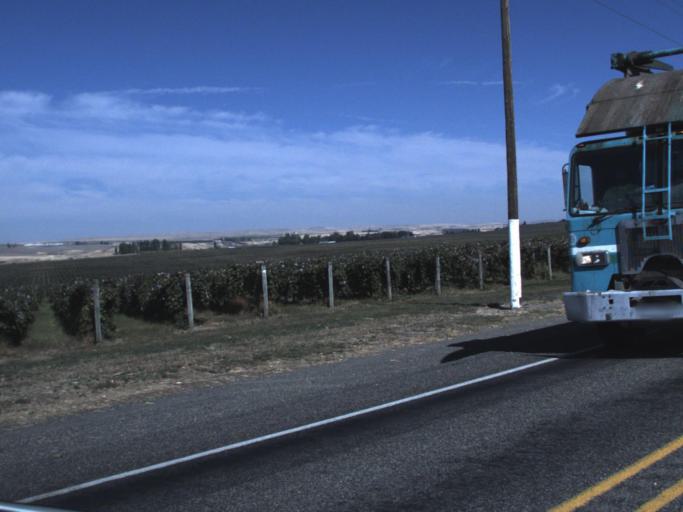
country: US
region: Washington
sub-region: Walla Walla County
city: Burbank
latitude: 46.2256
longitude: -118.8569
